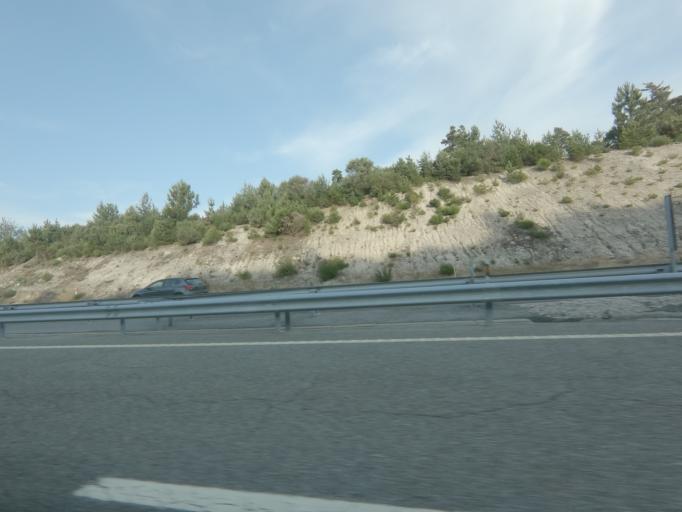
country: PT
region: Vila Real
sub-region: Vila Pouca de Aguiar
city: Vila Pouca de Aguiar
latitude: 41.4940
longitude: -7.6584
